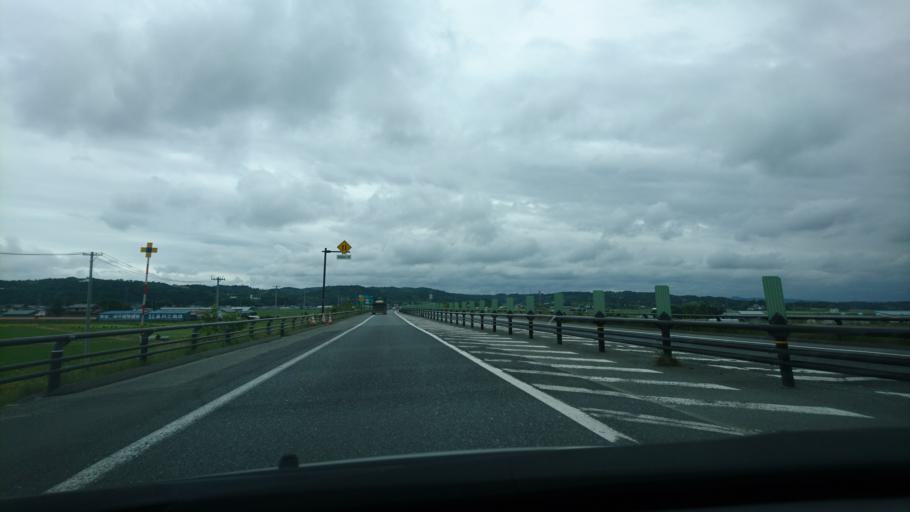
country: JP
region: Miyagi
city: Wakuya
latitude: 38.6647
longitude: 141.2655
